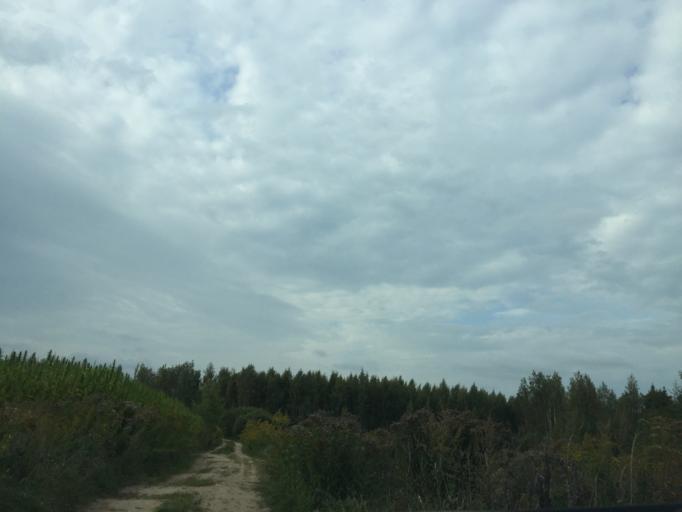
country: LV
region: Baldone
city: Baldone
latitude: 56.7642
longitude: 24.4664
